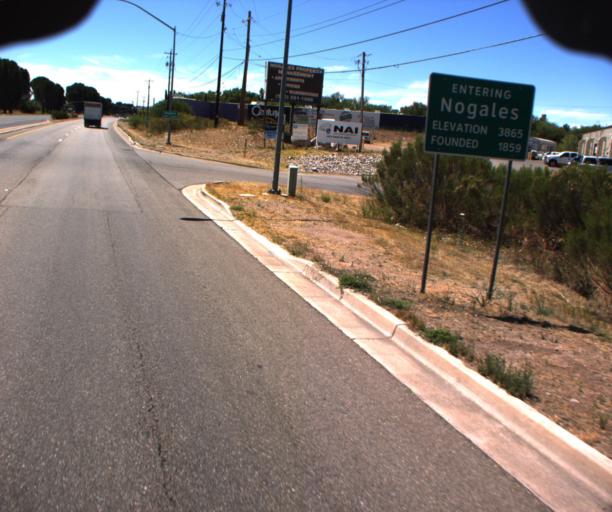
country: US
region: Arizona
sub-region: Santa Cruz County
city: Nogales
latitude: 31.3922
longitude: -110.9546
